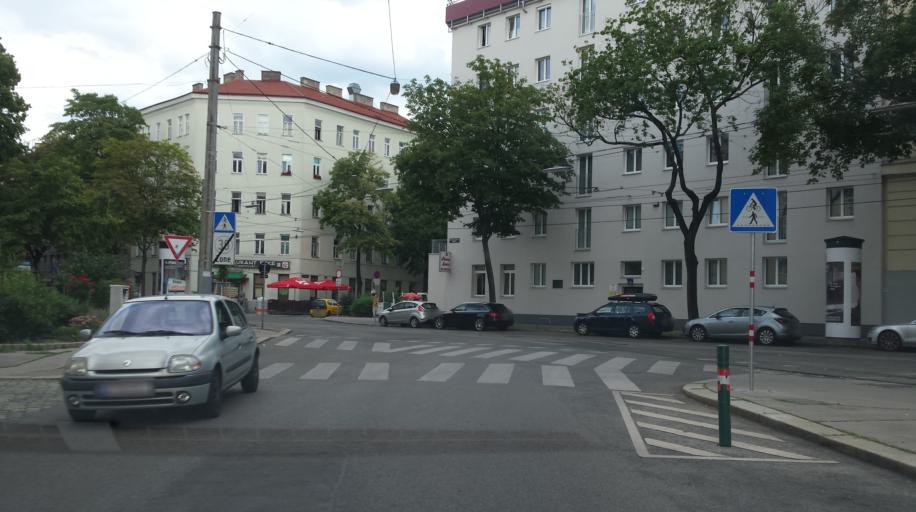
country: AT
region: Vienna
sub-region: Wien Stadt
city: Vienna
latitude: 48.1800
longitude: 16.3413
